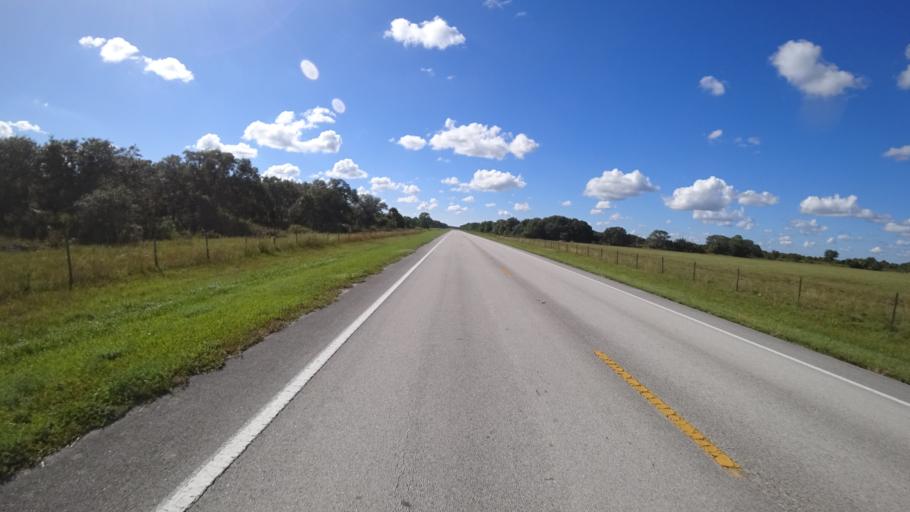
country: US
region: Florida
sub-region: Sarasota County
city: Warm Mineral Springs
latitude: 27.1935
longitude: -82.1758
